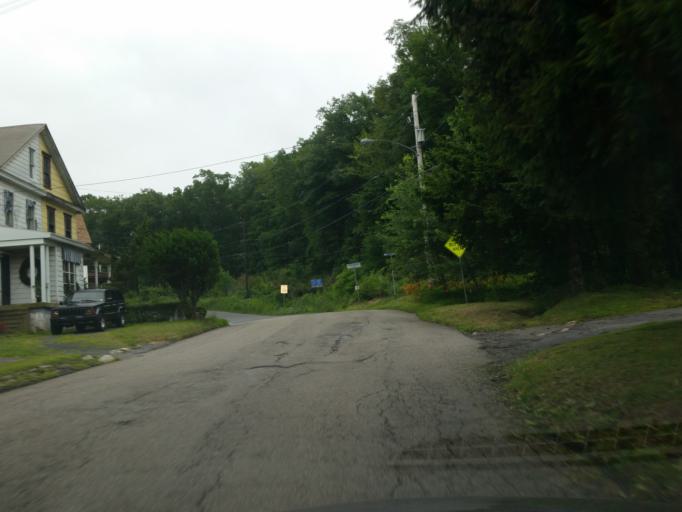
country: US
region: Pennsylvania
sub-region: Schuylkill County
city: Tremont
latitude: 40.6110
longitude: -76.4539
